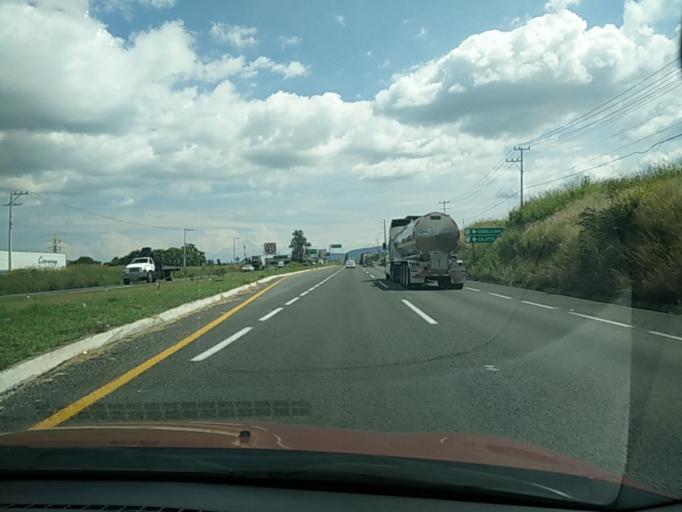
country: MX
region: Jalisco
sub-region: Ixtlahuacan de los Membrillos
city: Los Olivos
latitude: 20.4436
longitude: -103.2458
